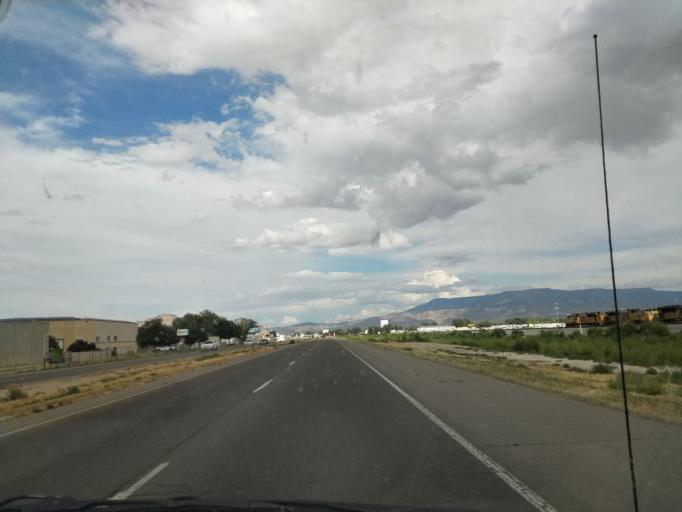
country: US
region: Colorado
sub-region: Mesa County
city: Fruitvale
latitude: 39.0744
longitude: -108.5080
